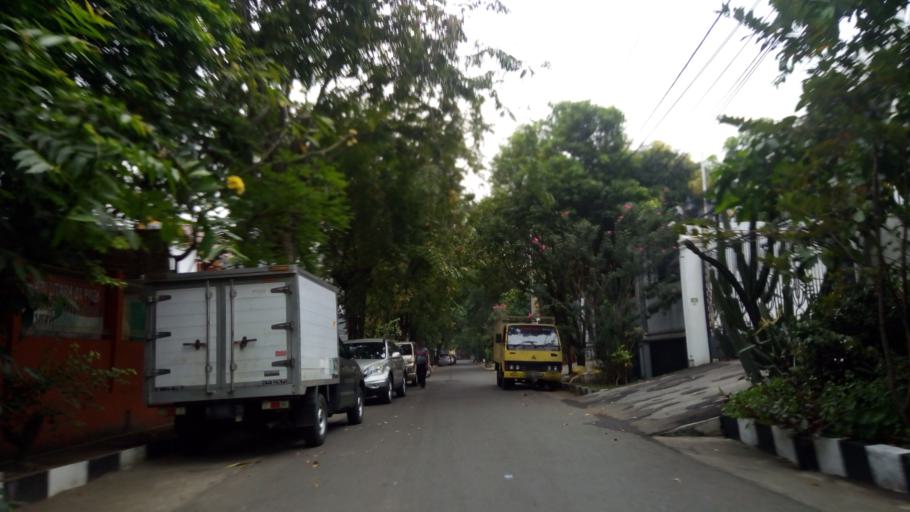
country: ID
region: Jakarta Raya
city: Jakarta
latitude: -6.1459
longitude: 106.8402
